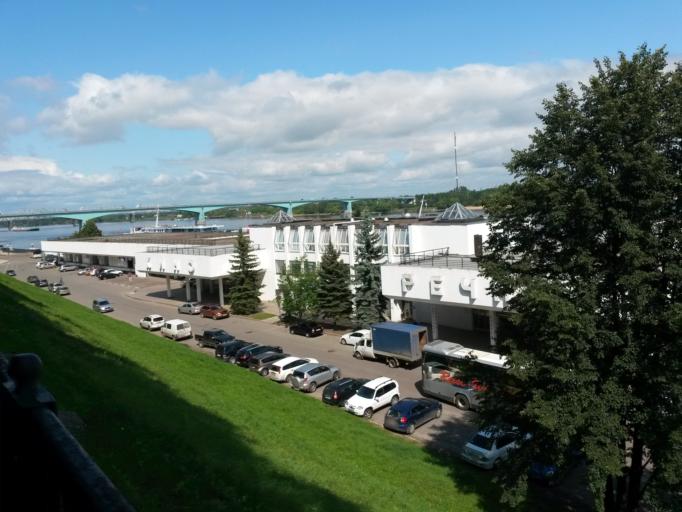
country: RU
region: Jaroslavl
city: Yaroslavl
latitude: 57.6336
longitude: 39.8928
